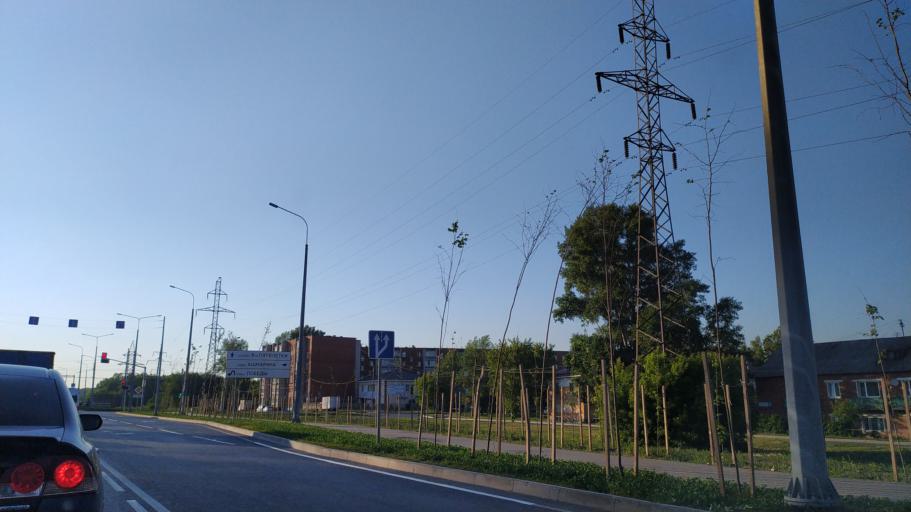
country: RU
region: Chuvashia
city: Kugesi
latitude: 56.0782
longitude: 47.2721
